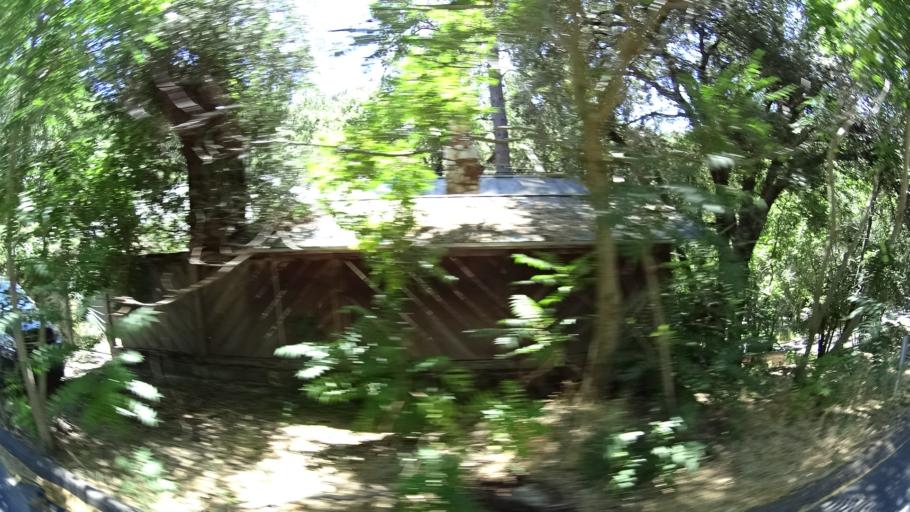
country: US
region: California
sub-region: Calaveras County
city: Murphys
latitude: 38.1212
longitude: -120.4965
